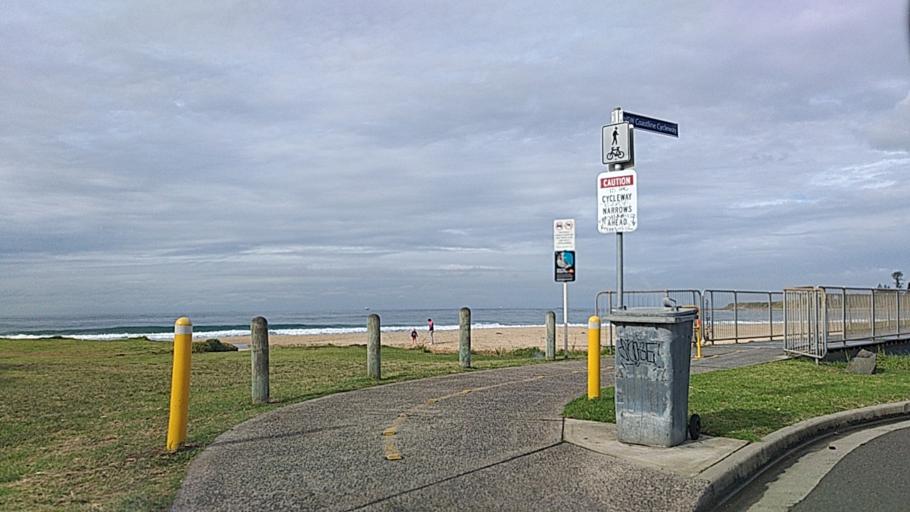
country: AU
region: New South Wales
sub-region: Wollongong
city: Bulli
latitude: -34.3234
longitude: 150.9238
